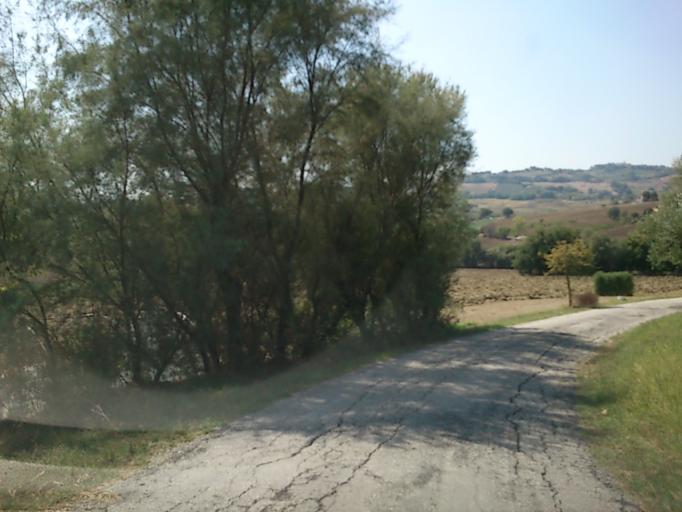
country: IT
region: The Marches
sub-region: Provincia di Pesaro e Urbino
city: Lucrezia
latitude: 43.7846
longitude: 12.9206
